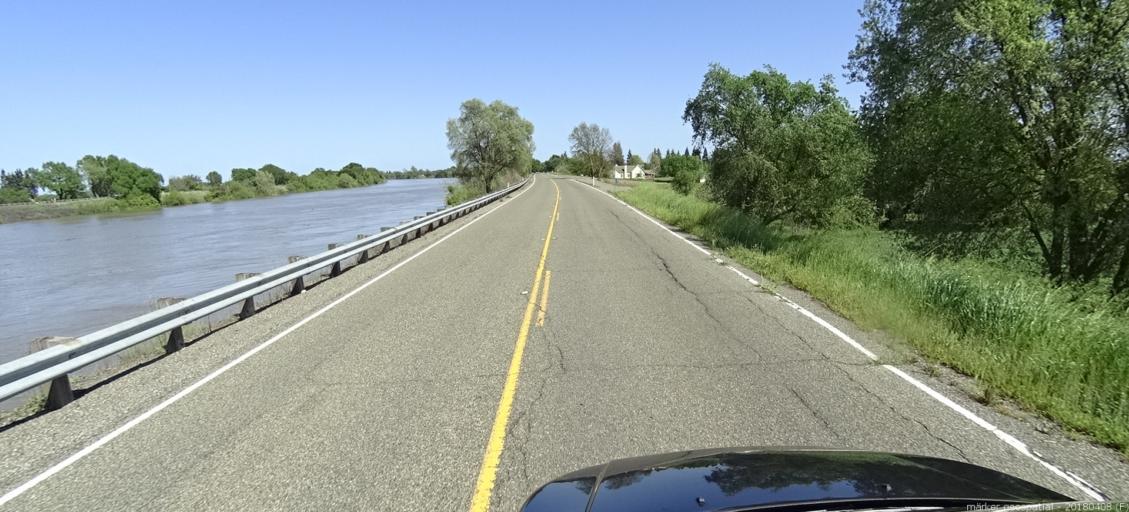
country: US
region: California
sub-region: Sacramento County
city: Parkway
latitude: 38.4340
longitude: -121.5223
